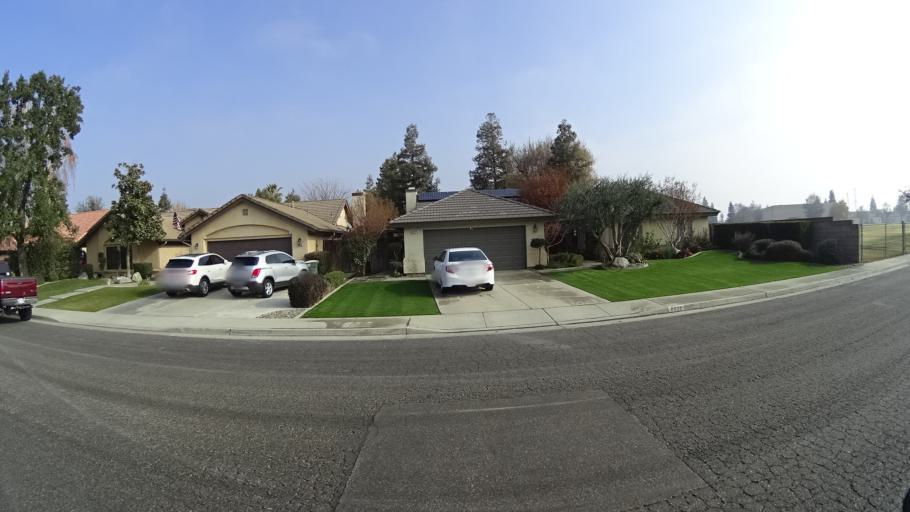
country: US
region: California
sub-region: Kern County
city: Greenacres
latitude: 35.3225
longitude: -119.1018
